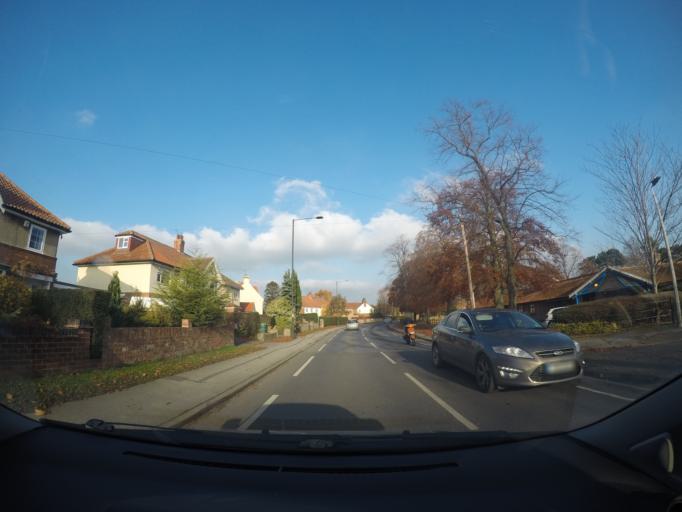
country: GB
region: England
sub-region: City of York
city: Huntington
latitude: 53.9912
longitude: -1.0661
